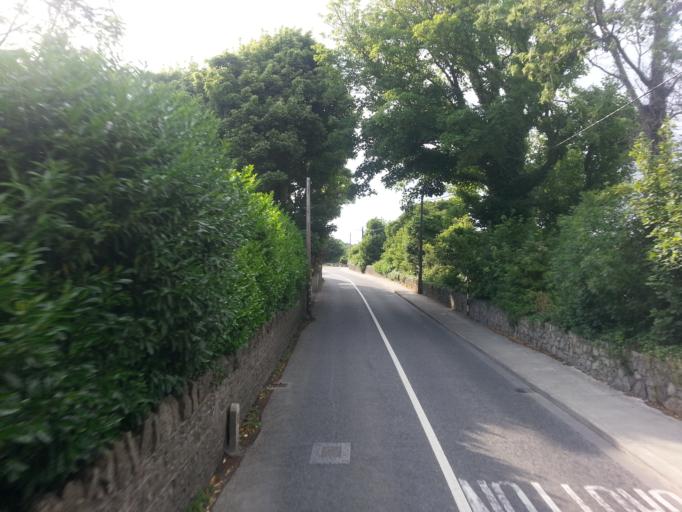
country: IE
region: Leinster
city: Foxrock
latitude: 53.2464
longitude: -6.2012
